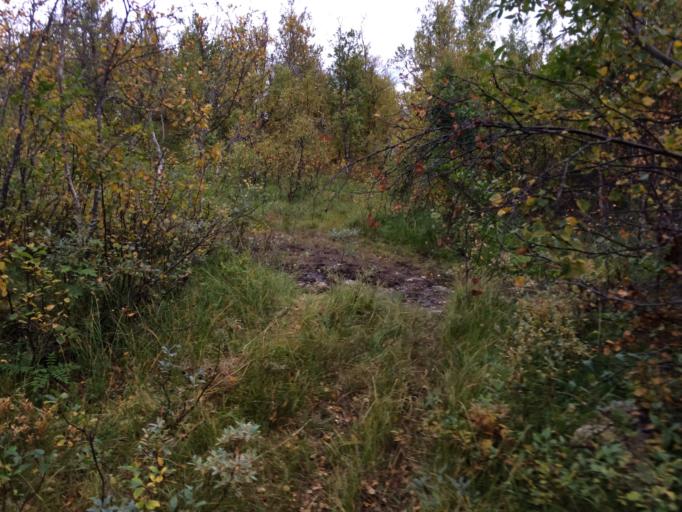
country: NO
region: Troms
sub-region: Sorreisa
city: Sorreisa
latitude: 69.5343
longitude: 18.3102
